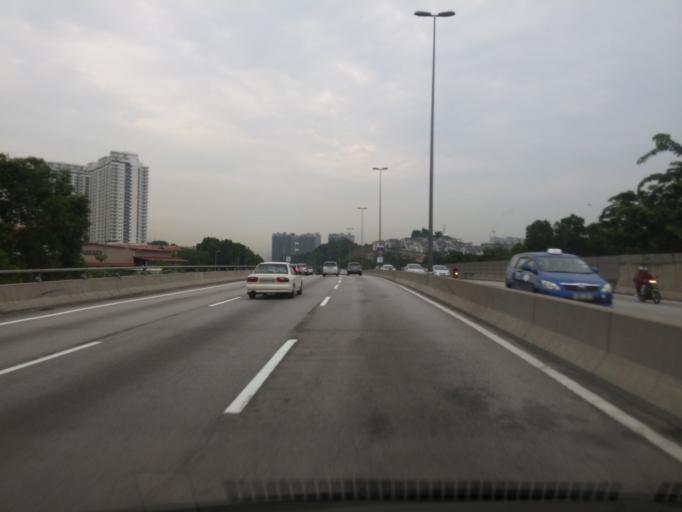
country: MY
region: Kuala Lumpur
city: Kuala Lumpur
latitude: 3.0738
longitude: 101.6885
